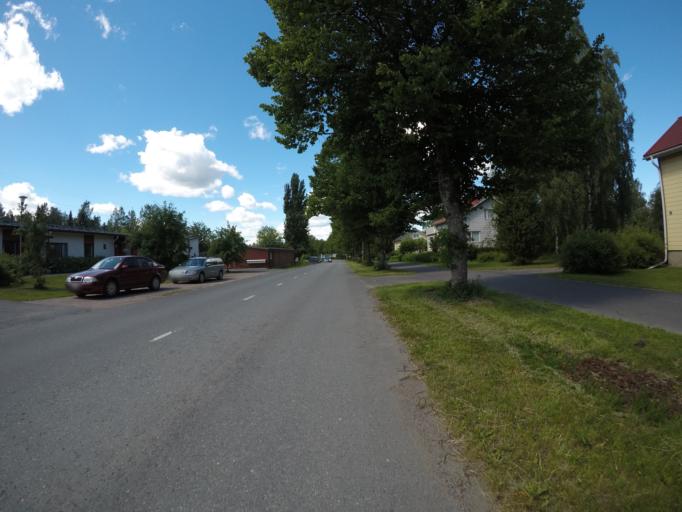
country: FI
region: Haeme
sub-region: Haemeenlinna
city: Haemeenlinna
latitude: 61.0187
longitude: 24.4357
